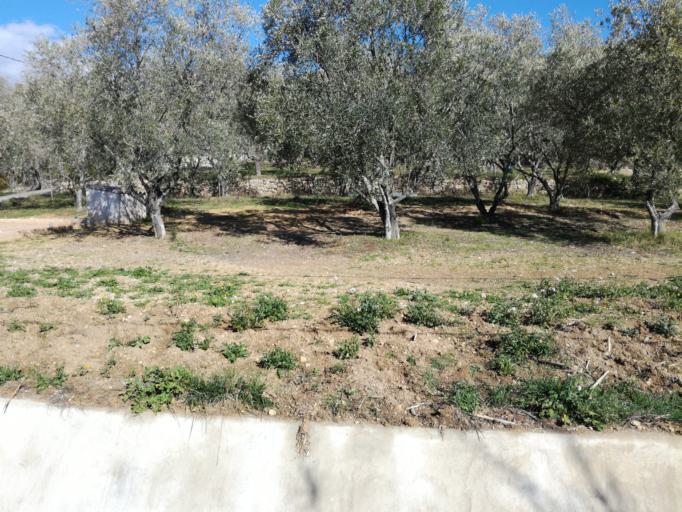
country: FR
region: Provence-Alpes-Cote d'Azur
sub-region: Departement des Alpes-Maritimes
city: Mouans-Sartoux
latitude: 43.6239
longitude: 6.9804
